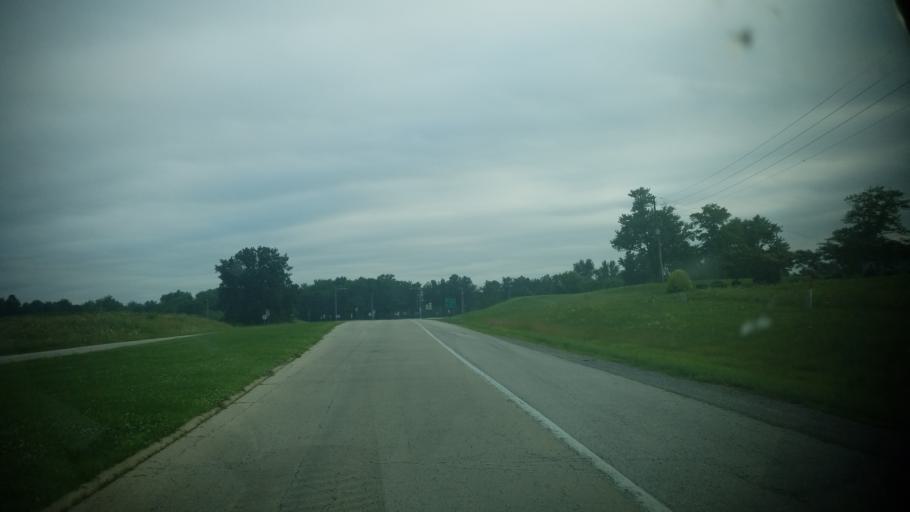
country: US
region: Illinois
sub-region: Clay County
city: Flora
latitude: 38.6717
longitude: -88.4381
